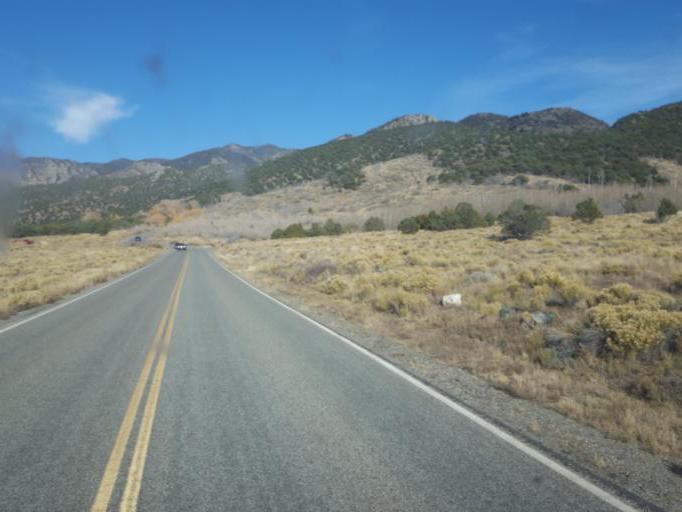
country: US
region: Colorado
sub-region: Custer County
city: Westcliffe
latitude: 37.7308
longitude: -105.5137
